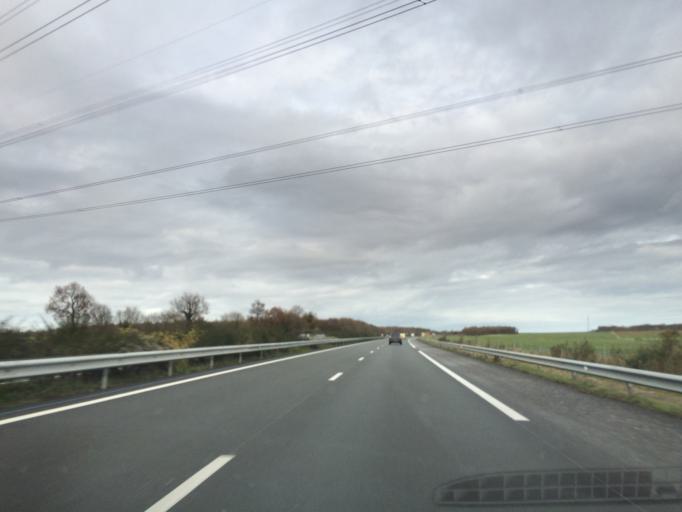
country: FR
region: Poitou-Charentes
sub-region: Departement des Deux-Sevres
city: Beauvoir-sur-Niort
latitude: 46.1714
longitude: -0.5089
